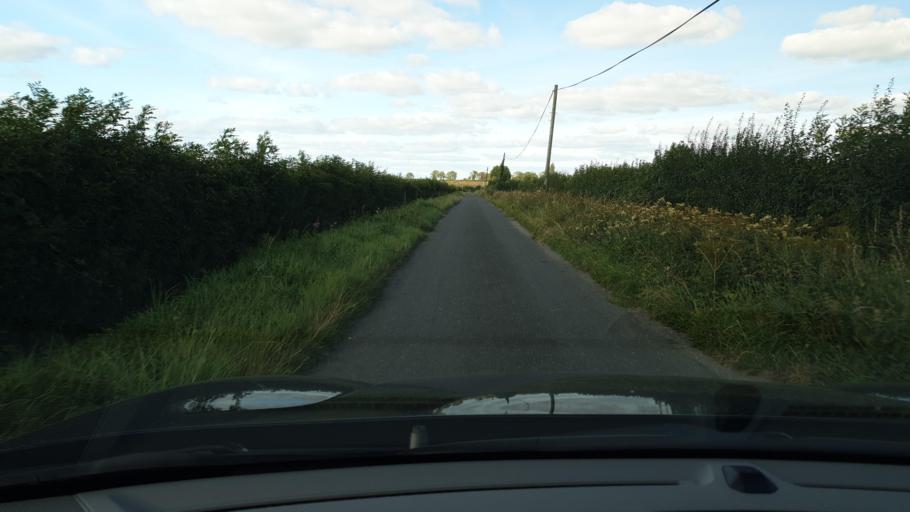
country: IE
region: Leinster
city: Hartstown
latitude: 53.4399
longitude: -6.4302
